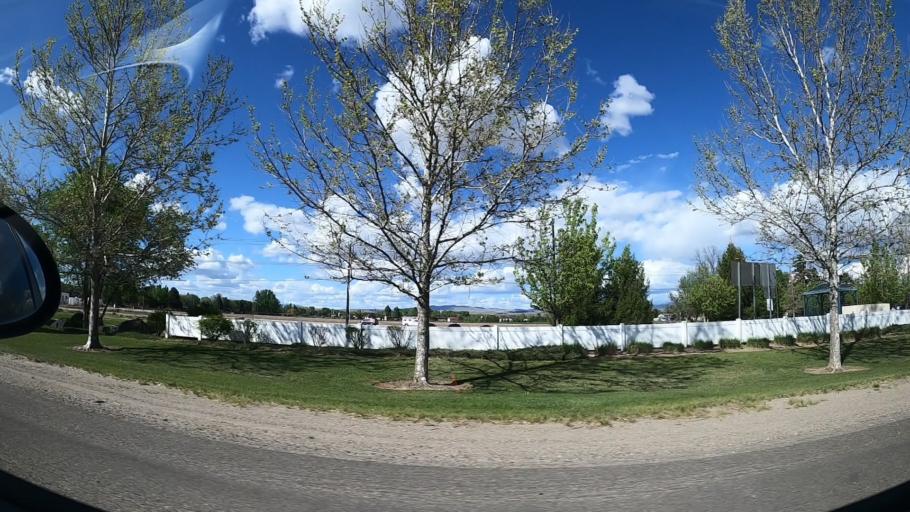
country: US
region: Idaho
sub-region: Ada County
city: Eagle
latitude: 43.6949
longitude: -116.3772
